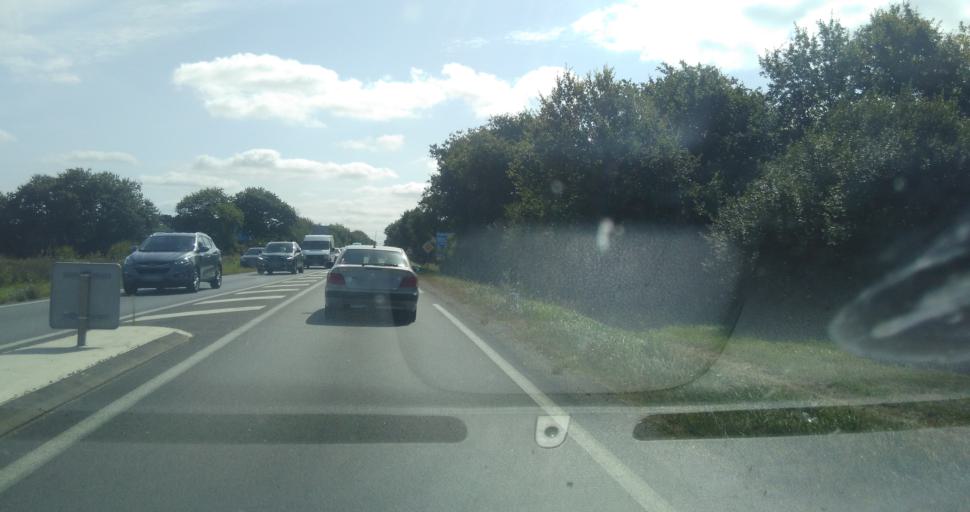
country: FR
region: Pays de la Loire
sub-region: Departement de la Vendee
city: Chateau-d'Olonne
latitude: 46.4787
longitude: -1.6868
